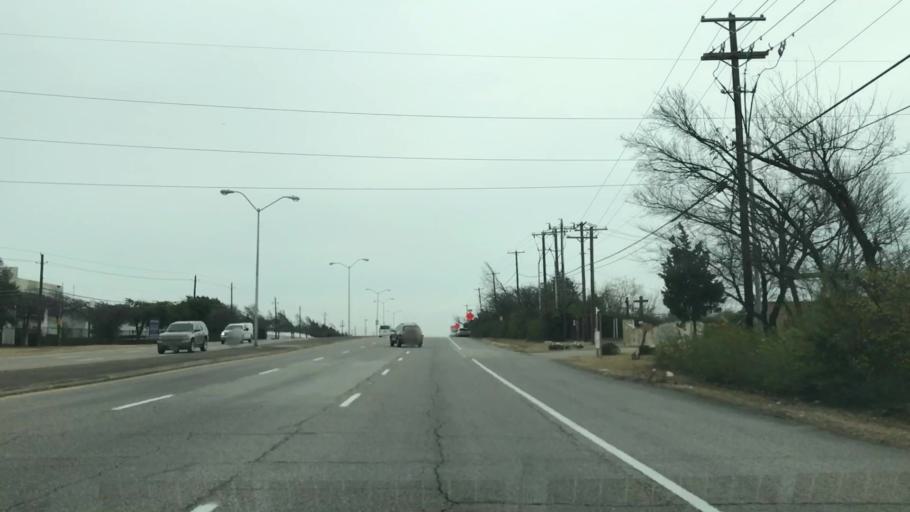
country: US
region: Texas
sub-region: Dallas County
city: Cockrell Hill
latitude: 32.7496
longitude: -96.8965
